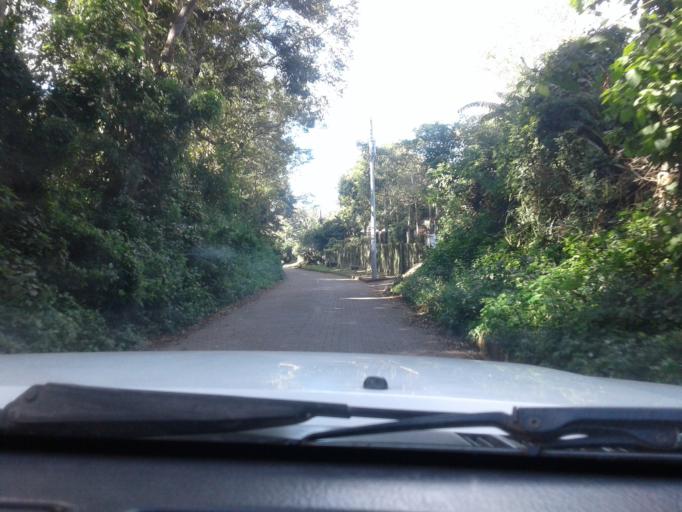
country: NI
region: Carazo
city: Dolores
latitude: 11.8523
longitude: -86.2225
